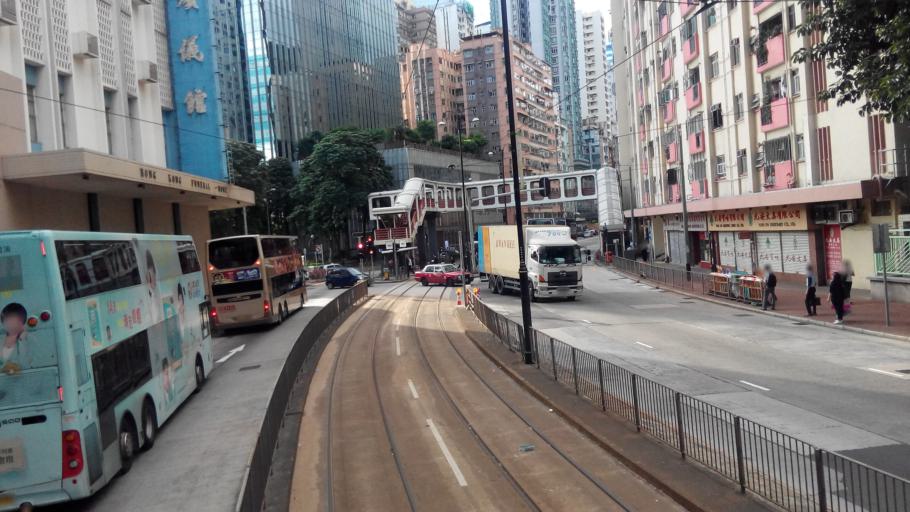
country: HK
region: Kowloon City
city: Kowloon
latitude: 22.2912
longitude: 114.2087
